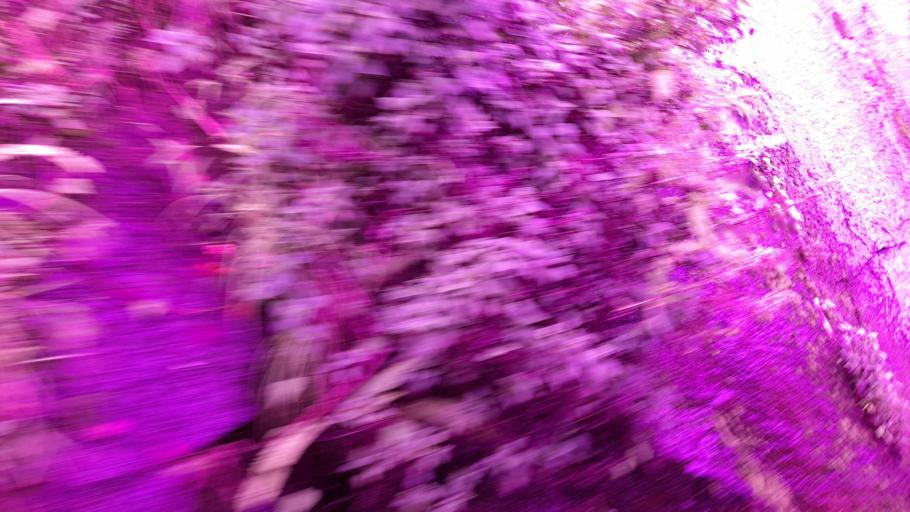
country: NP
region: Central Region
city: Kirtipur
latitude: 27.8308
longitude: 85.2046
